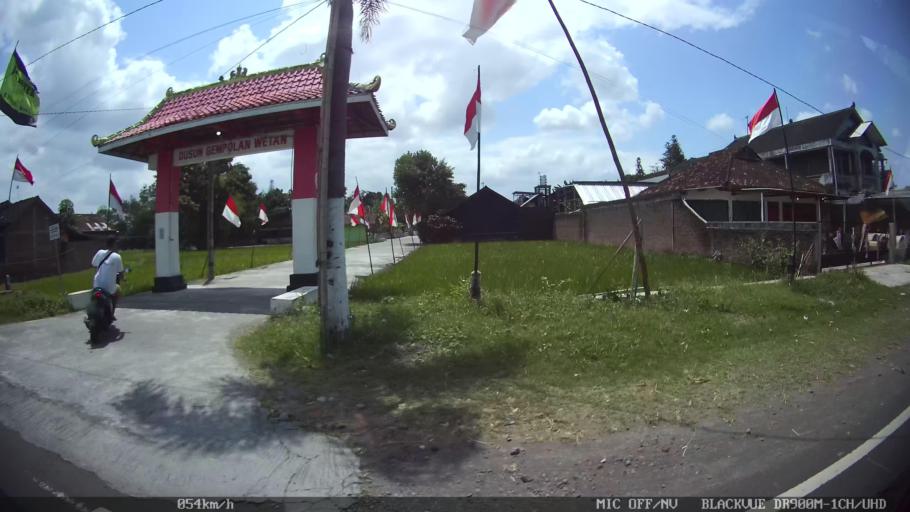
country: ID
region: Daerah Istimewa Yogyakarta
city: Sewon
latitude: -7.8829
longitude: 110.3464
